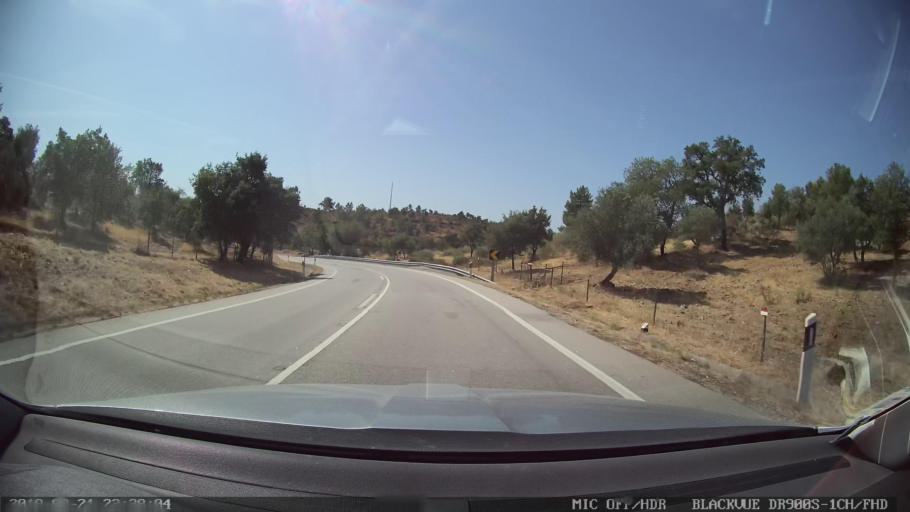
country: PT
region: Guarda
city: Alcains
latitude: 39.8624
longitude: -7.3555
